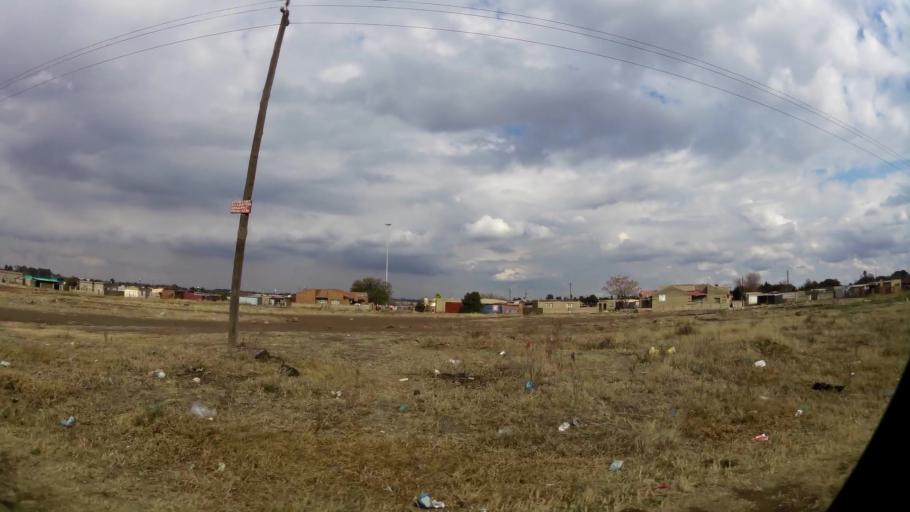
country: ZA
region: Gauteng
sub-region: Sedibeng District Municipality
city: Vanderbijlpark
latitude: -26.7000
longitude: 27.7950
